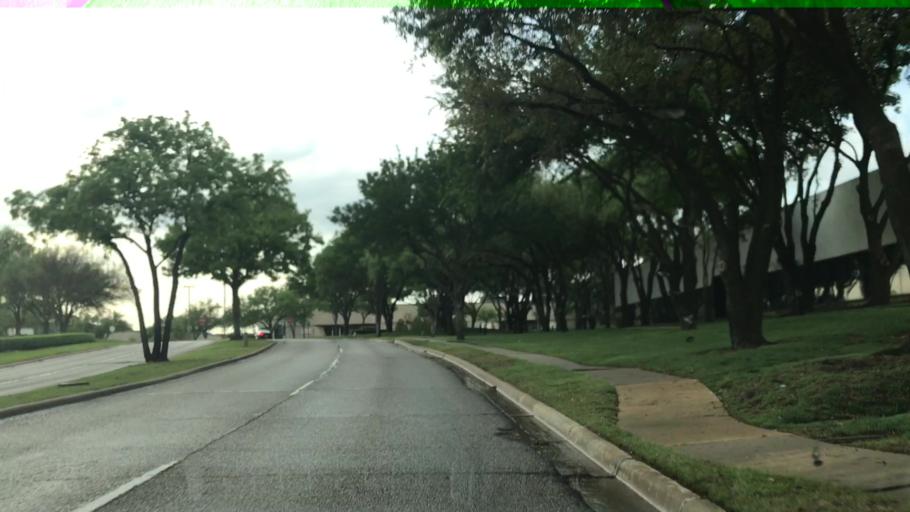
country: US
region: Texas
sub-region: Dallas County
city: Irving
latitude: 32.8707
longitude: -96.9816
